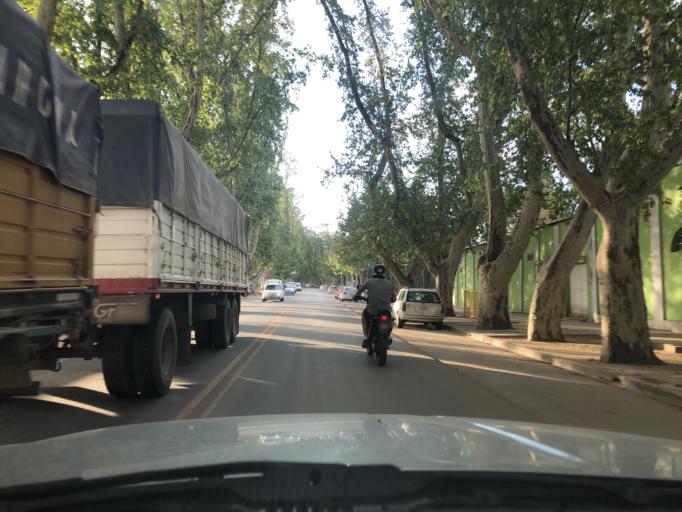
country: AR
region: Cordoba
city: Jesus Maria
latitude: -30.9991
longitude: -64.0877
